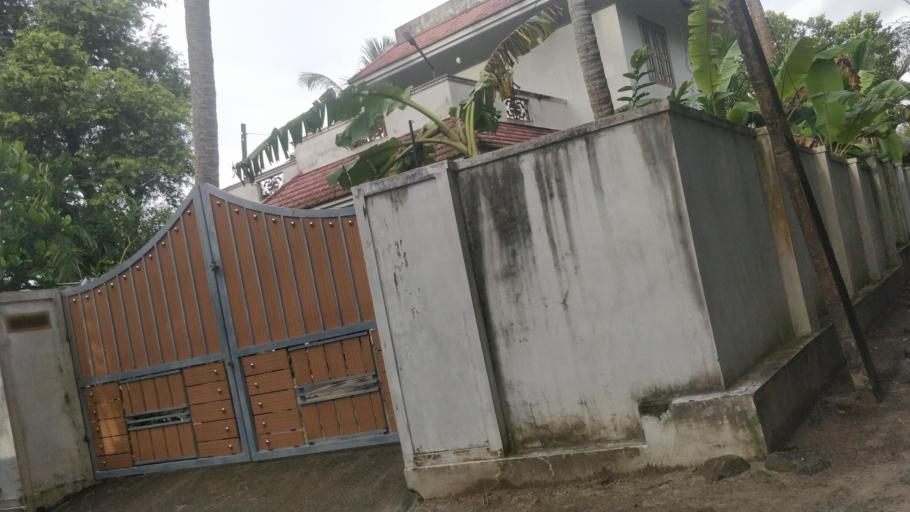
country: IN
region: Kerala
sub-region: Alappuzha
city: Shertallai
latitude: 9.6903
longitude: 76.3601
